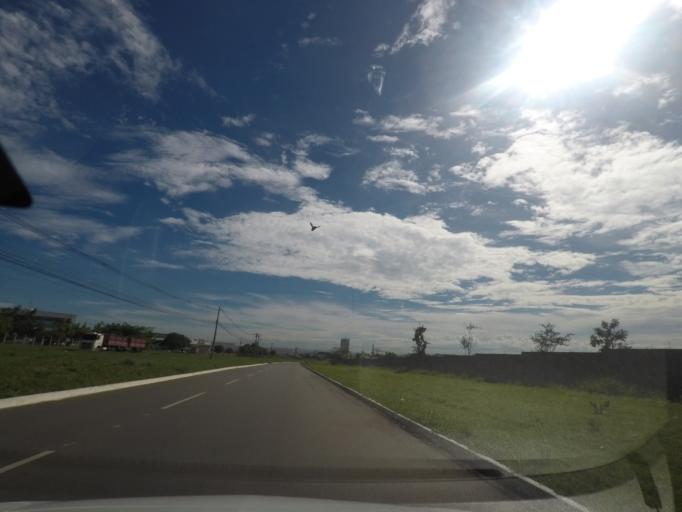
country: BR
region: Goias
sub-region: Aparecida De Goiania
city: Aparecida de Goiania
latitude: -16.8023
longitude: -49.2599
